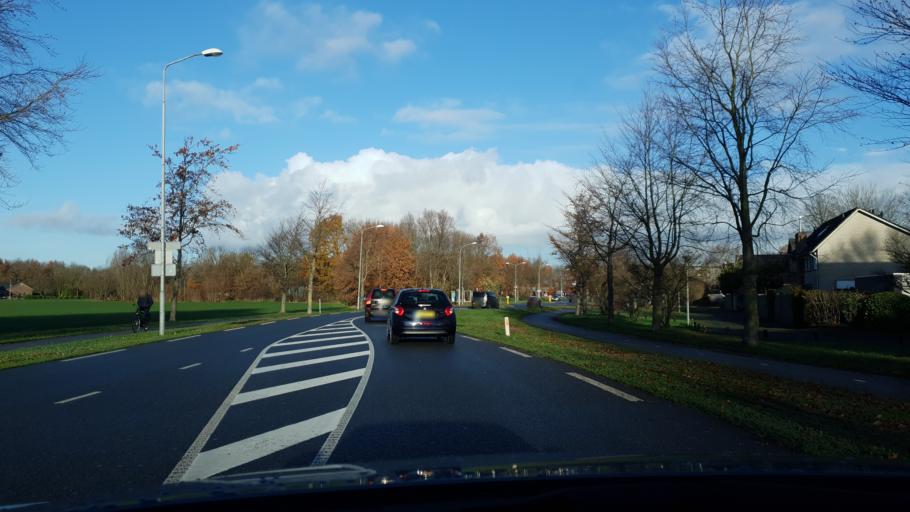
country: NL
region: Gelderland
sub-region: Gemeente Wijchen
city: Wijchen
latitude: 51.8093
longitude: 5.7036
